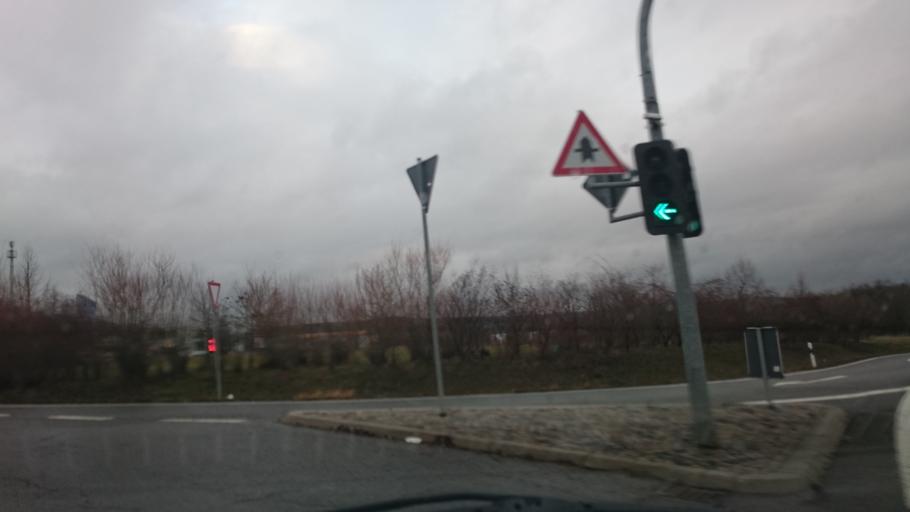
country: DE
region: Saxony
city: Sankt Egidien
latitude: 50.7707
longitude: 12.6223
